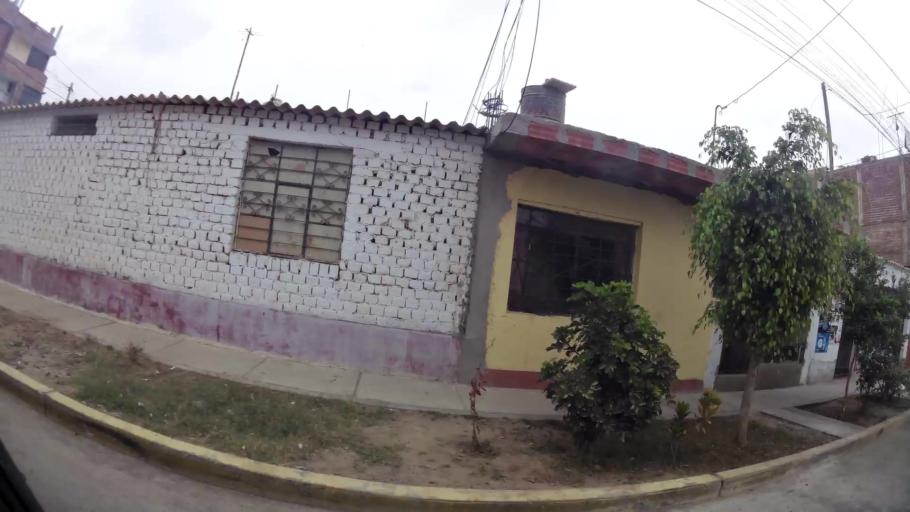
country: PE
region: La Libertad
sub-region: Provincia de Trujillo
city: Trujillo
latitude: -8.1219
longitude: -79.0262
